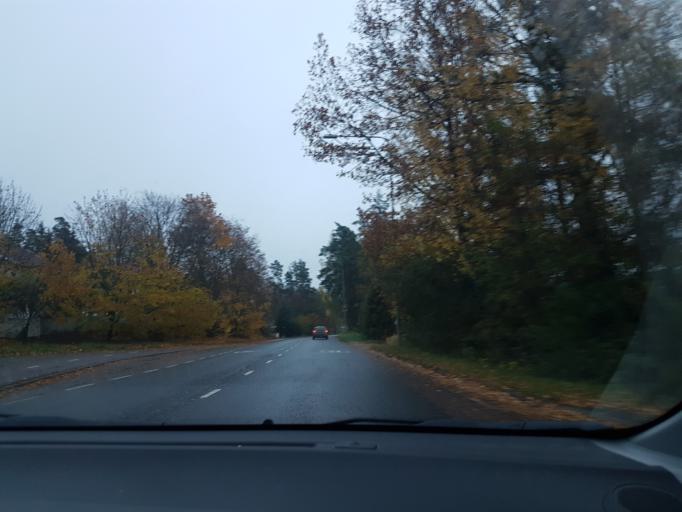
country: FI
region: Uusimaa
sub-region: Helsinki
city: Tuusula
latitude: 60.4054
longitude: 25.0128
